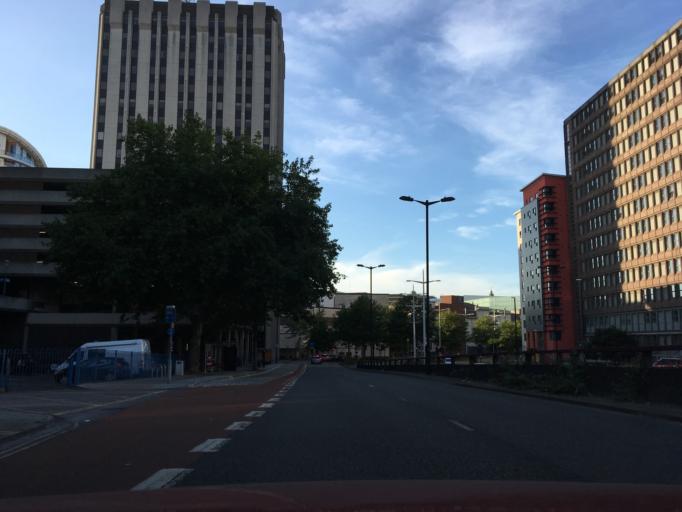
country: GB
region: England
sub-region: Bristol
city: Bristol
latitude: 51.4561
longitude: -2.5841
